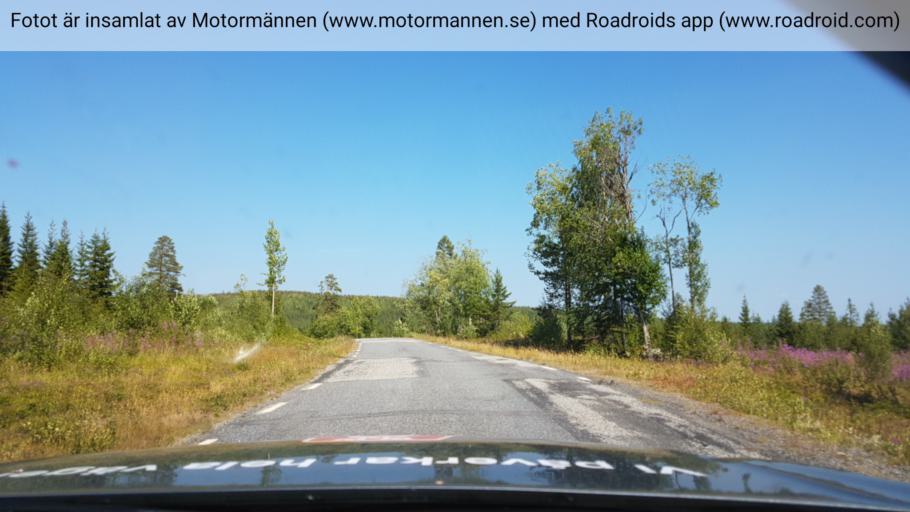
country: SE
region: Vaesterbotten
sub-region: Dorotea Kommun
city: Dorotea
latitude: 64.0616
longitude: 16.5563
